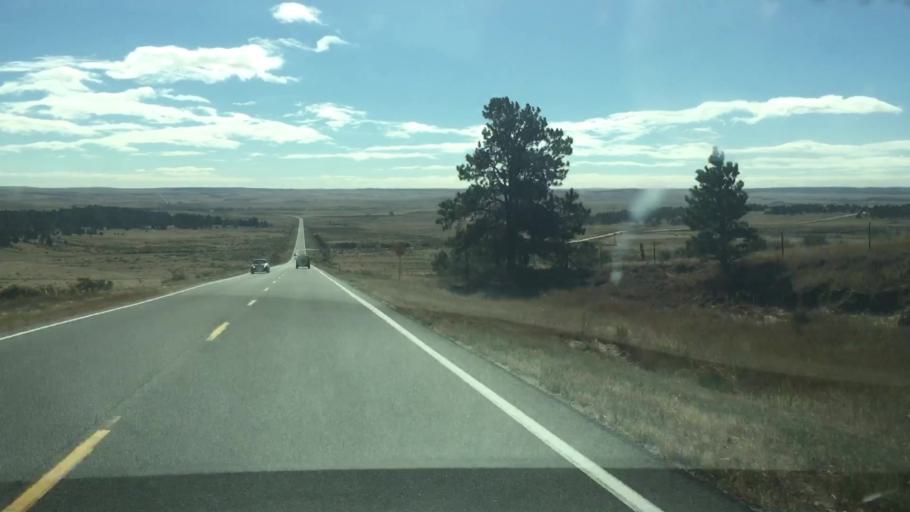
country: US
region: Colorado
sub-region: Elbert County
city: Kiowa
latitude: 39.3119
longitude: -104.3633
